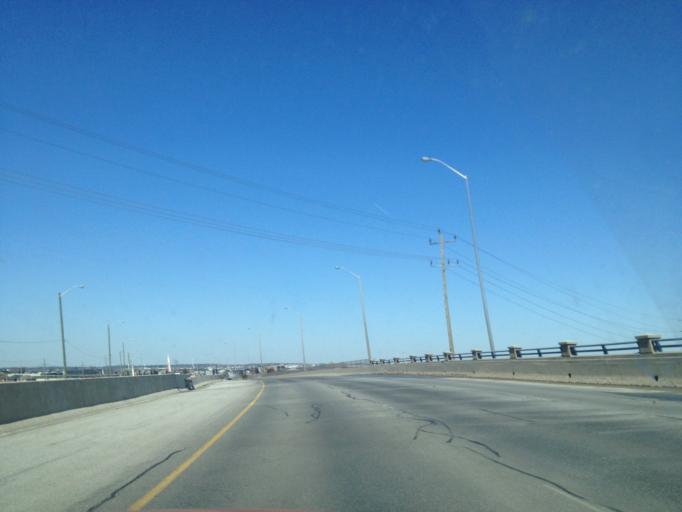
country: CA
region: Ontario
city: Brampton
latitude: 43.6759
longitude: -79.8173
